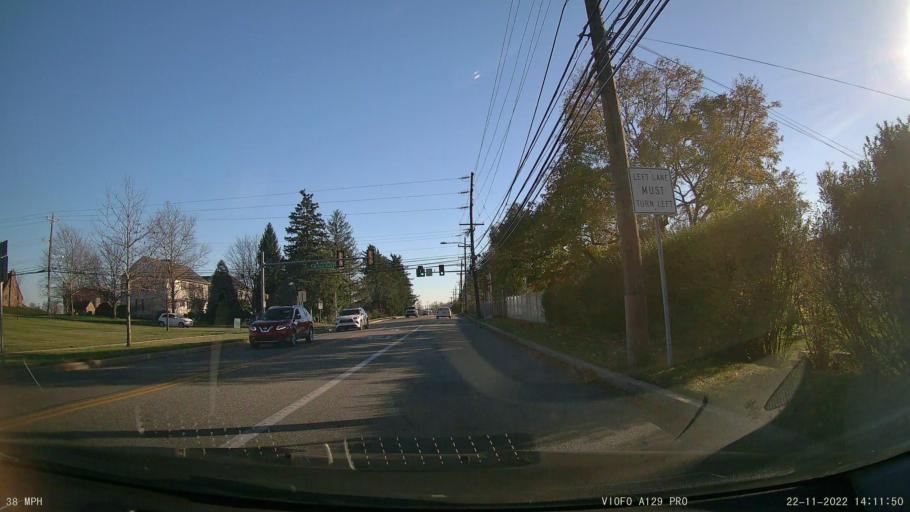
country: US
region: Pennsylvania
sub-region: Montgomery County
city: Bridgeport
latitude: 40.1004
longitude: -75.3683
